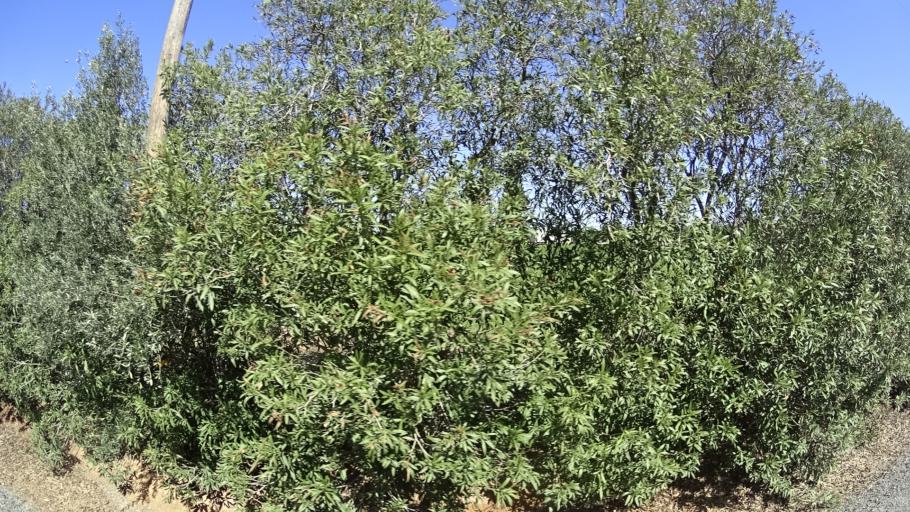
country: US
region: California
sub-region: Glenn County
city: Hamilton City
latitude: 39.7897
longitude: -122.0828
